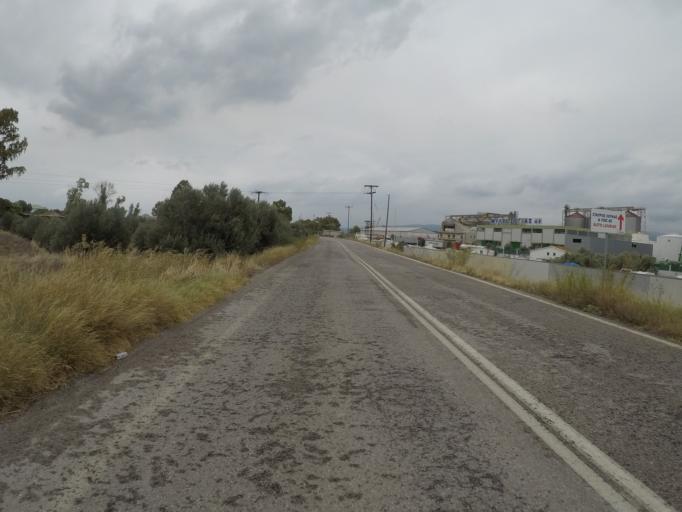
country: GR
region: Peloponnese
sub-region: Nomos Korinthias
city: Isthmia
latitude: 37.9226
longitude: 23.0222
